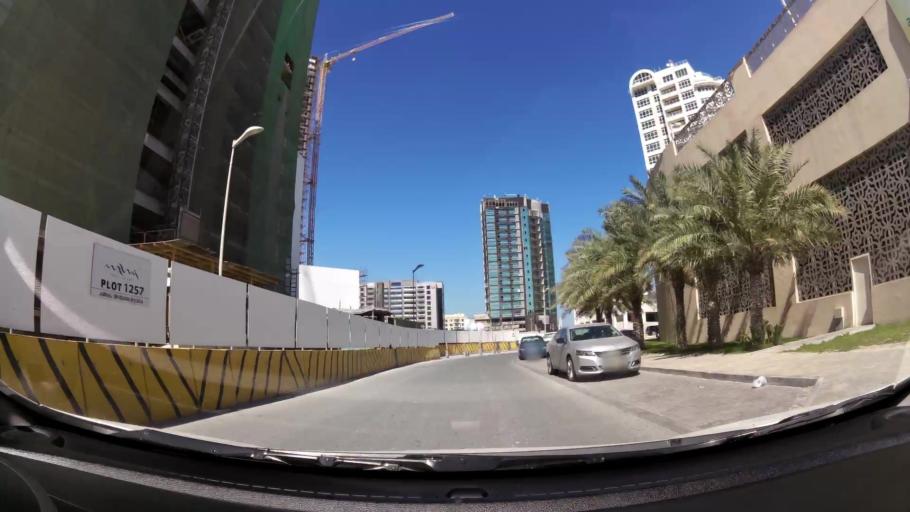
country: BH
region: Muharraq
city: Al Hadd
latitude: 26.2902
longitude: 50.6631
